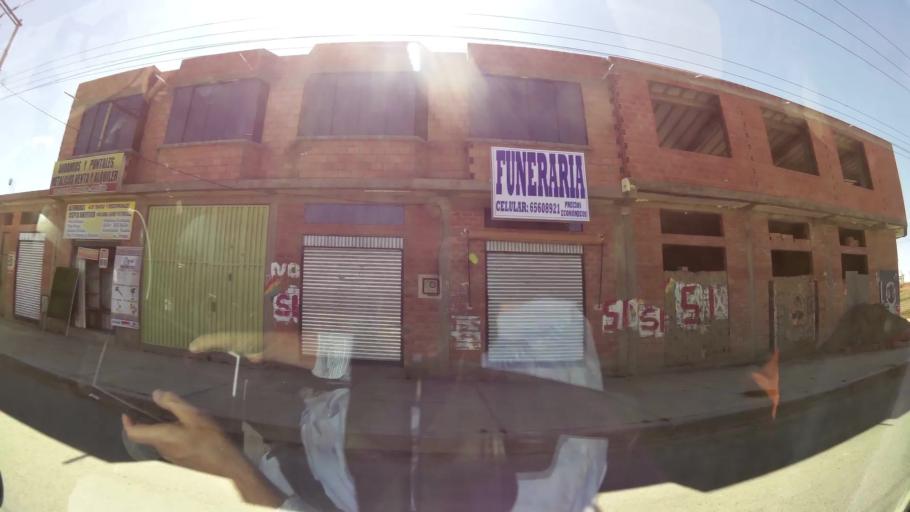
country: BO
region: La Paz
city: La Paz
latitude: -16.5203
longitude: -68.2216
